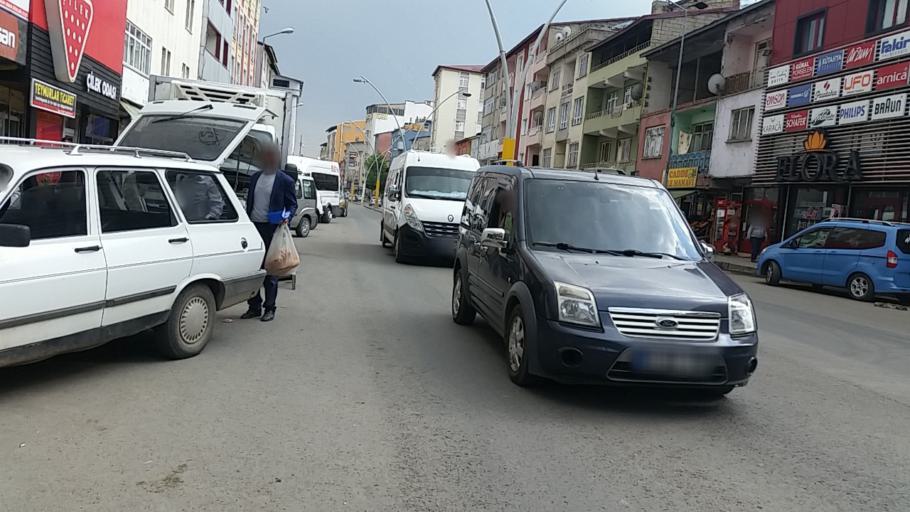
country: TR
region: Agri
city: Agri
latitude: 39.7237
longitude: 43.0513
